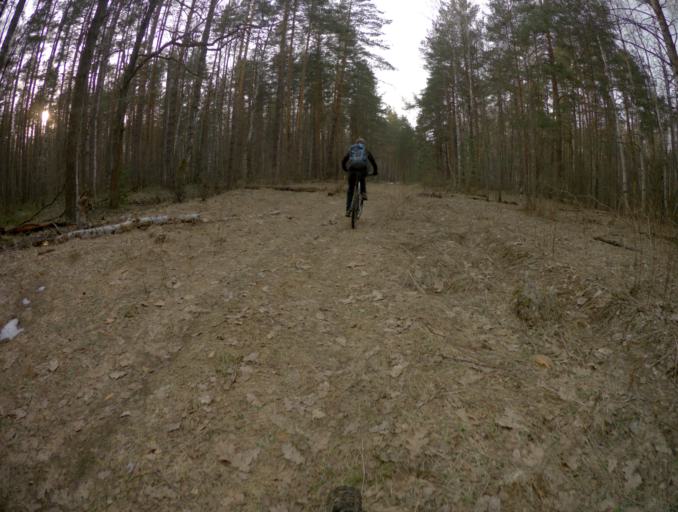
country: RU
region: Vladimir
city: Kommunar
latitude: 56.0750
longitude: 40.4449
